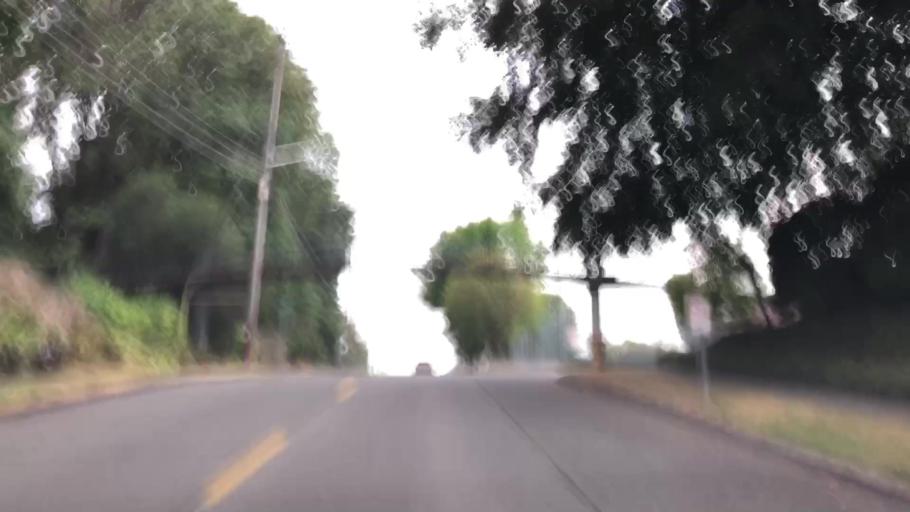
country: US
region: Washington
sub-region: King County
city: Yarrow Point
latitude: 47.6613
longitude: -122.2768
